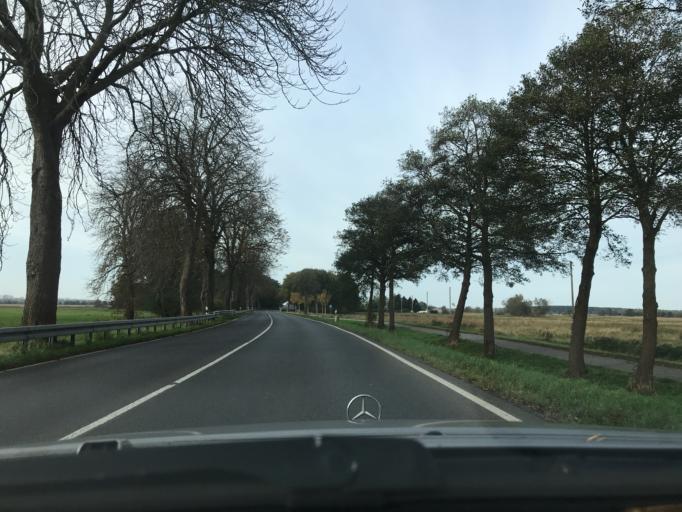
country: DE
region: Mecklenburg-Vorpommern
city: Ostseebad Zinnowitz
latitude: 54.0683
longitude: 13.8947
